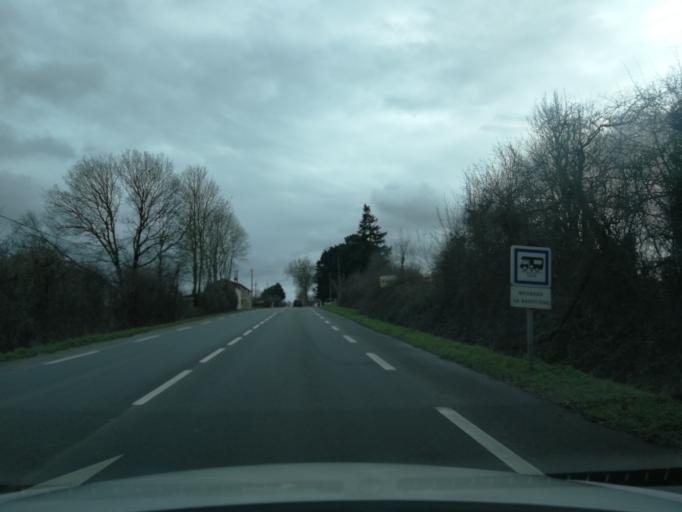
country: FR
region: Pays de la Loire
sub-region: Departement de la Vendee
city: Saint-Fulgent
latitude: 46.8677
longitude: -1.1942
